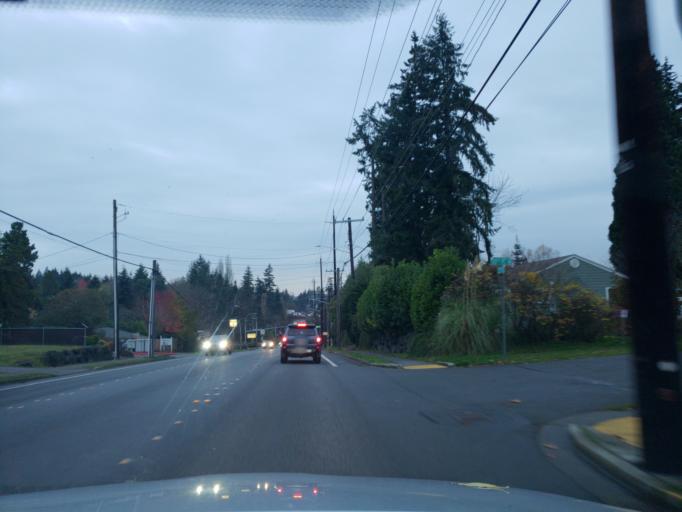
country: US
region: Washington
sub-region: Snohomish County
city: Mountlake Terrace
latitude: 47.8066
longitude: -122.3008
